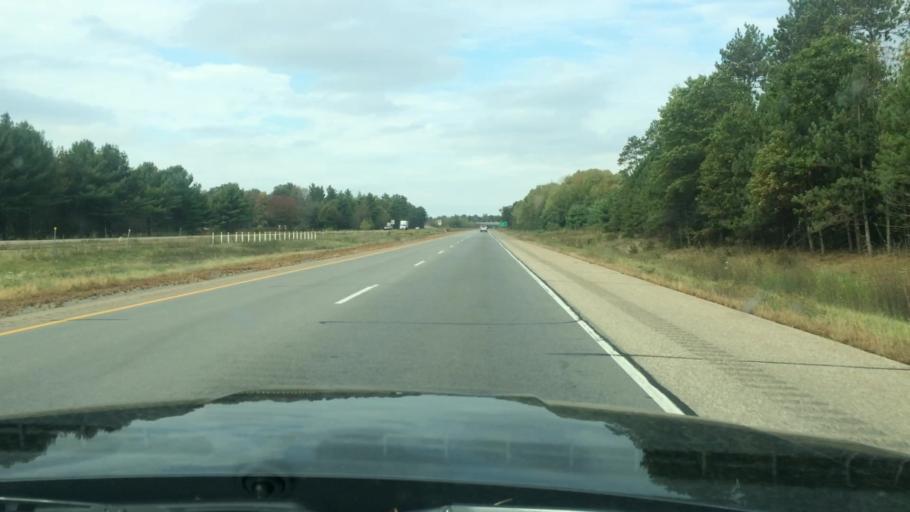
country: US
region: Wisconsin
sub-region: Marathon County
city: Mosinee
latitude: 44.7211
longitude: -89.6681
